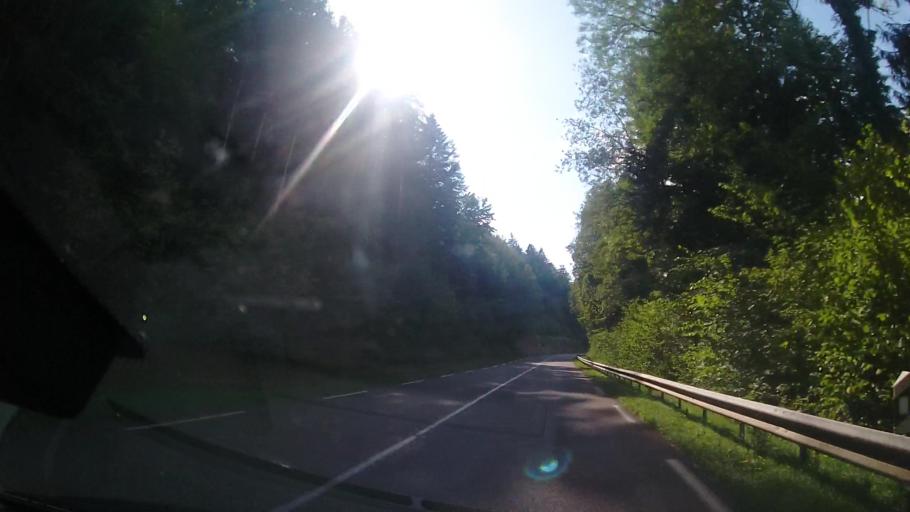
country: FR
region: Franche-Comte
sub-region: Departement du Jura
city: Clairvaux-les-Lacs
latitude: 46.5834
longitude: 5.8170
